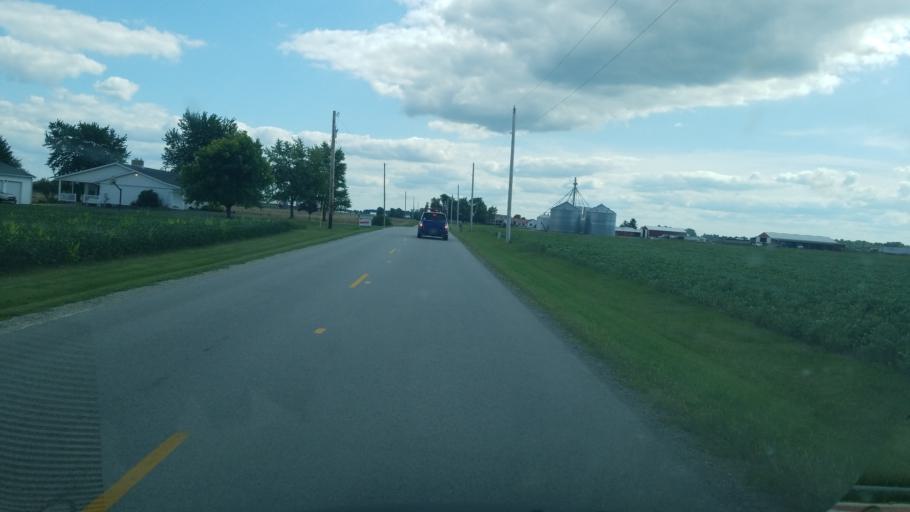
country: US
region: Ohio
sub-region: Logan County
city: Lakeview
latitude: 40.5846
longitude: -83.9756
